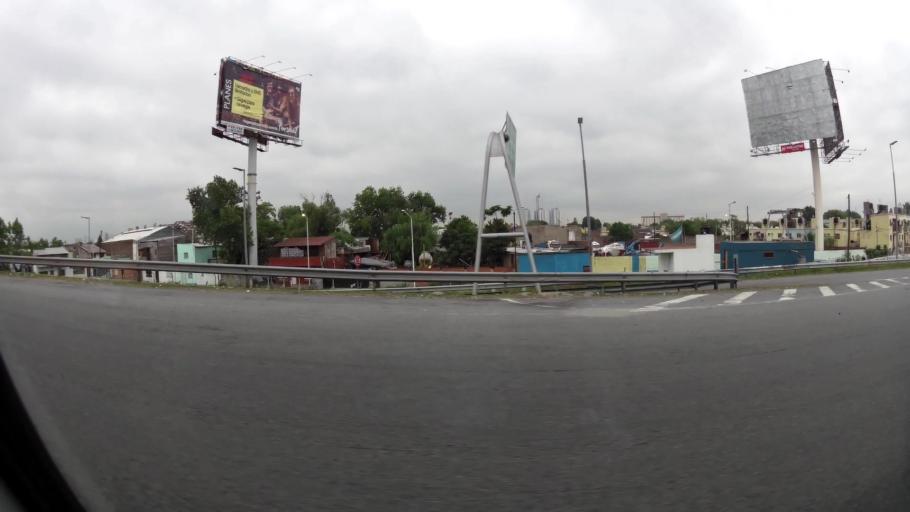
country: AR
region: Buenos Aires
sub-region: Partido de Avellaneda
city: Avellaneda
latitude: -34.6531
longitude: -58.3531
